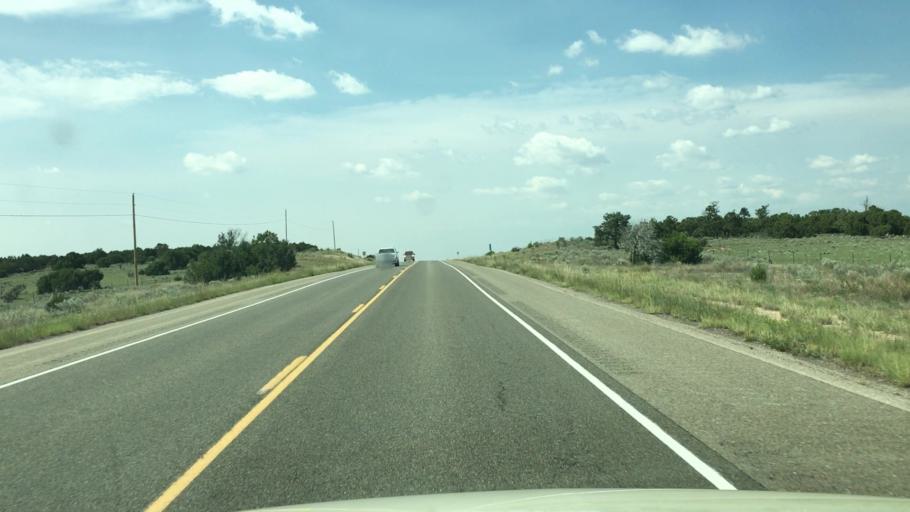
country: US
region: New Mexico
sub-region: Torrance County
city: Moriarty
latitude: 35.0427
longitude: -105.6834
